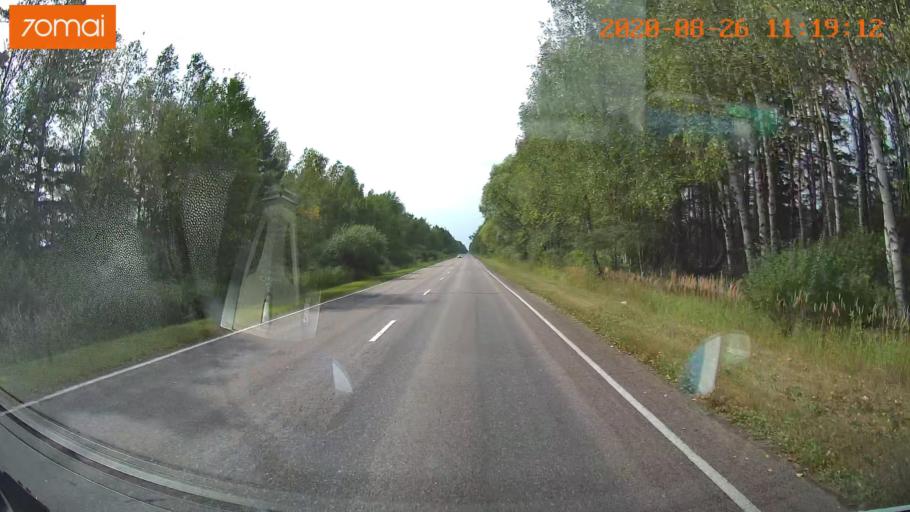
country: RU
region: Rjazan
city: Shilovo
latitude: 54.4019
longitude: 41.0840
